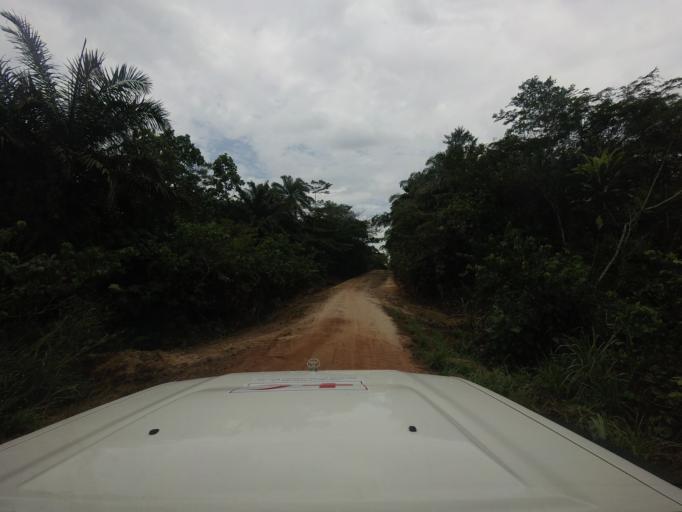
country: SL
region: Eastern Province
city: Buedu
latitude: 8.2897
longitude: -10.1993
